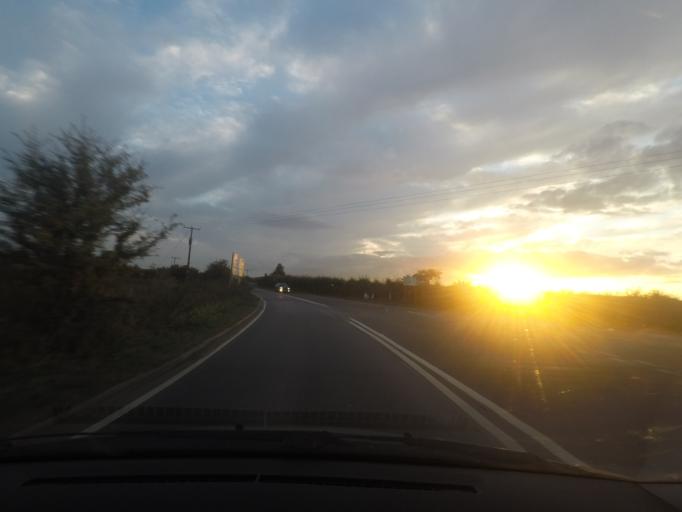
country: GB
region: England
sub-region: North Lincolnshire
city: Croxton
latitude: 53.5850
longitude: -0.3661
